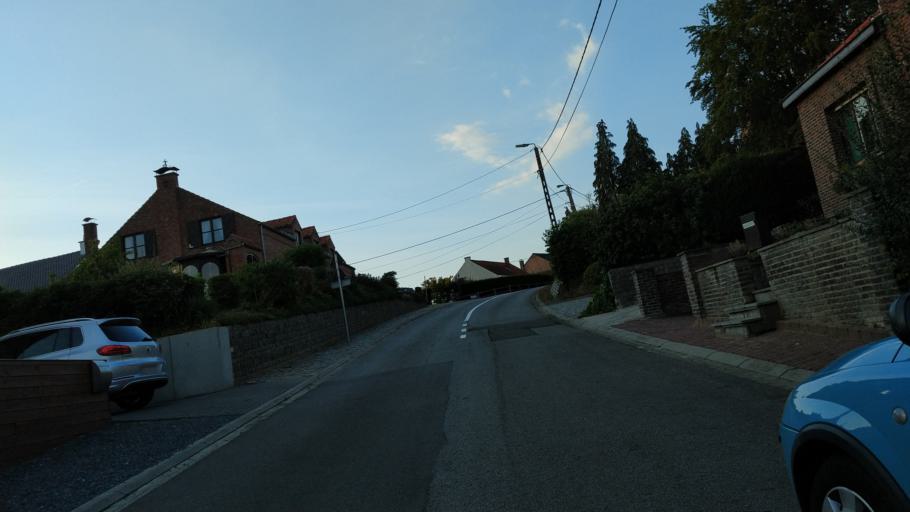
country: BE
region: Flanders
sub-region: Provincie Vlaams-Brabant
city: Oud-Heverlee
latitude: 50.8415
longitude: 4.6639
